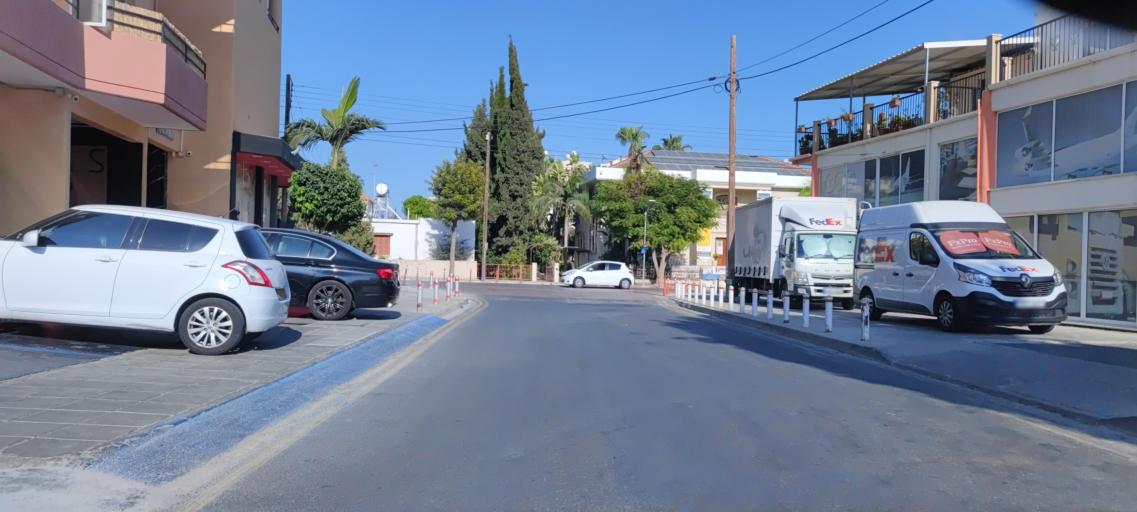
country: CY
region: Limassol
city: Mouttagiaka
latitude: 34.6950
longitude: 33.0805
